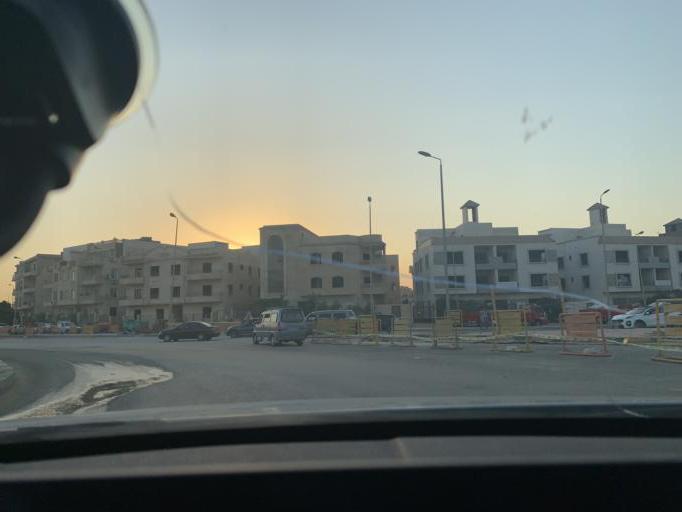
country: EG
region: Muhafazat al Qahirah
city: Cairo
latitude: 29.9999
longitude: 31.4688
